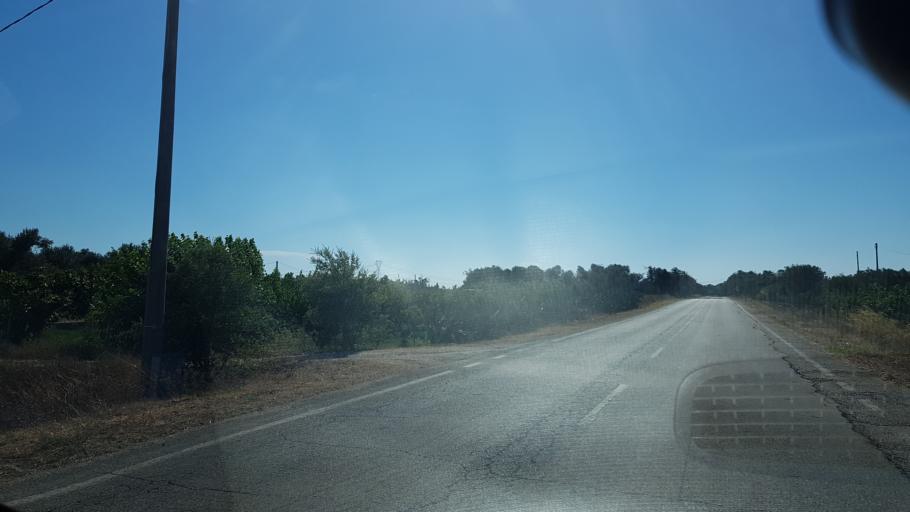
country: IT
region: Apulia
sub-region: Provincia di Brindisi
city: Tuturano
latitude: 40.5505
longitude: 17.8854
